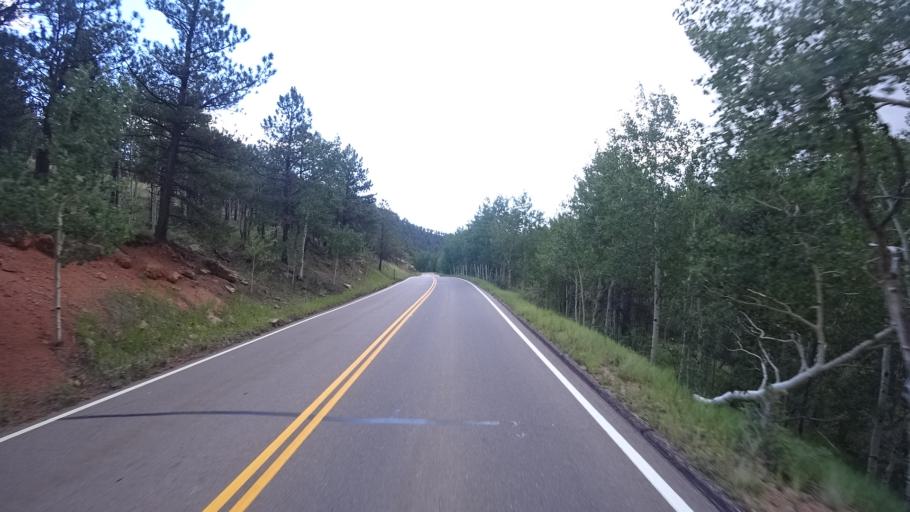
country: US
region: Colorado
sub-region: El Paso County
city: Cascade-Chipita Park
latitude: 38.9099
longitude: -105.0173
